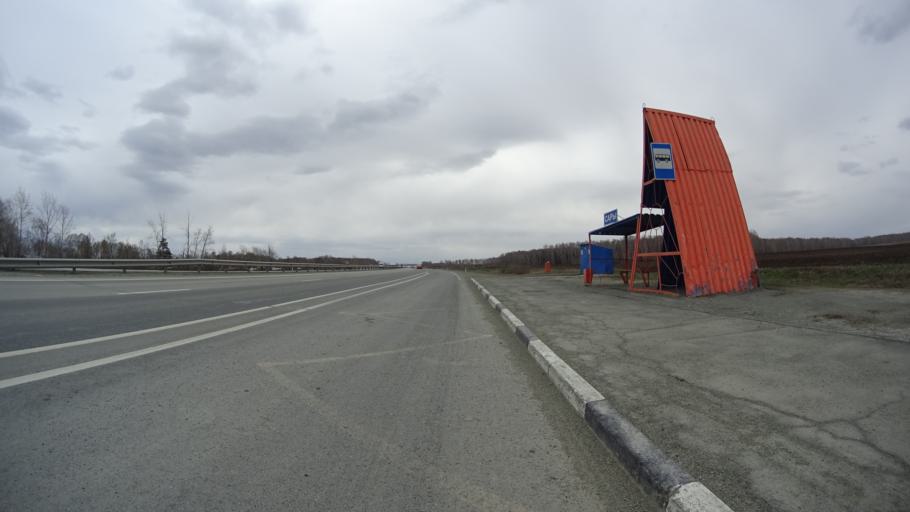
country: RU
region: Chelyabinsk
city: Yemanzhelinka
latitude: 54.8237
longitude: 61.3094
